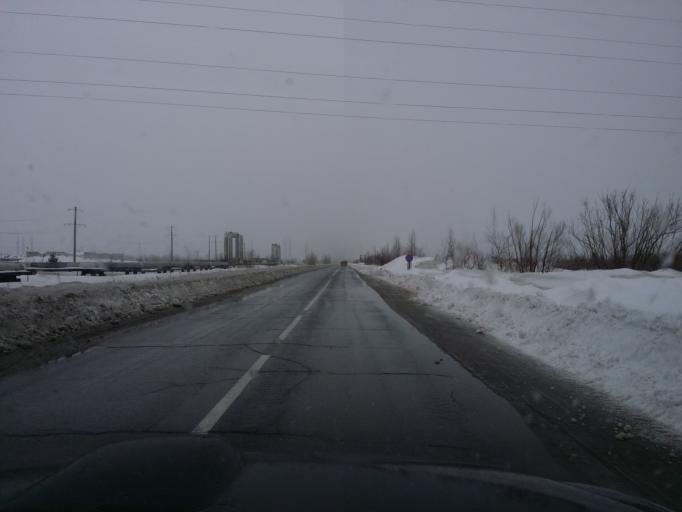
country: RU
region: Khanty-Mansiyskiy Avtonomnyy Okrug
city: Izluchinsk
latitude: 60.9786
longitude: 76.9010
